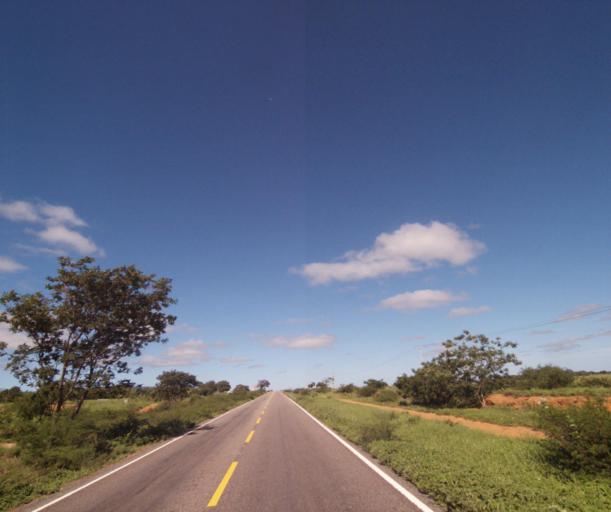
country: BR
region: Bahia
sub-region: Palmas De Monte Alto
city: Palmas de Monte Alto
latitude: -14.2375
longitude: -43.0121
